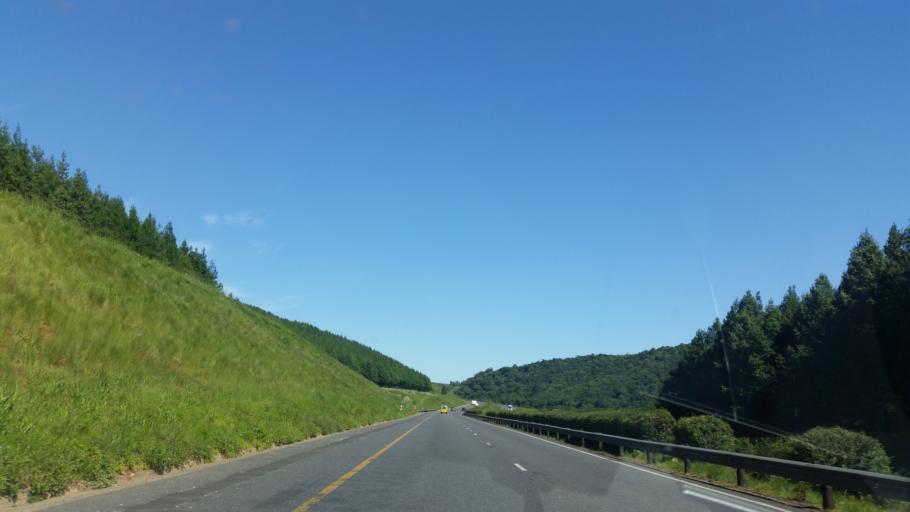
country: ZA
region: KwaZulu-Natal
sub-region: uMgungundlovu District Municipality
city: Mooirivier
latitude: -29.3434
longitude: 30.0812
